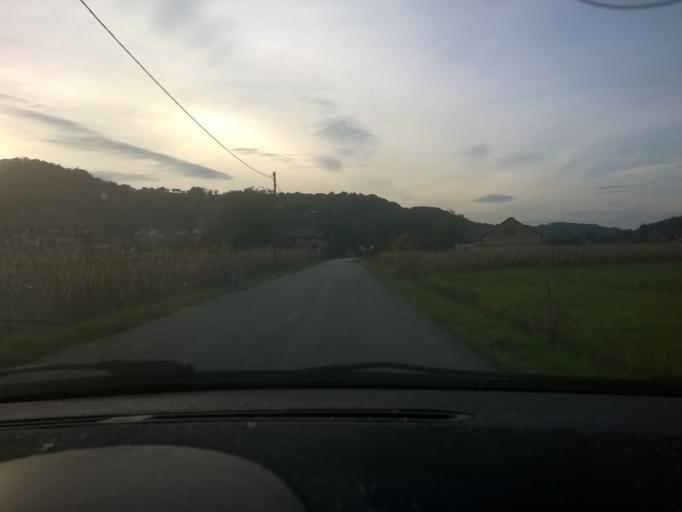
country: HR
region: Krapinsko-Zagorska
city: Zabok
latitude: 46.0785
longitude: 15.9016
